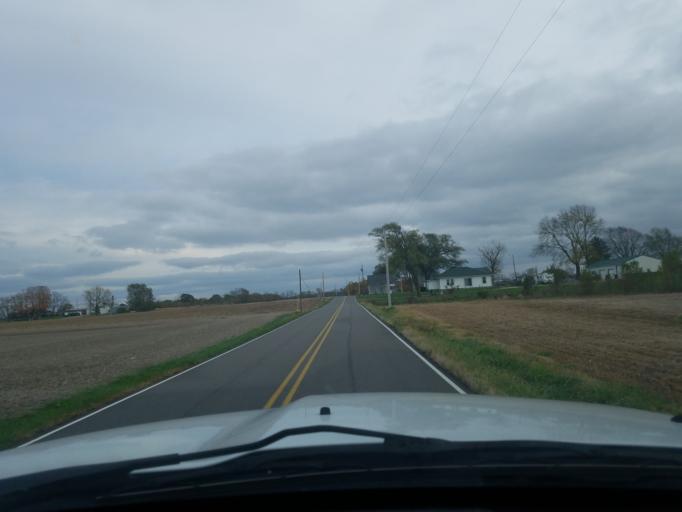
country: US
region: Indiana
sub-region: Shelby County
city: Shelbyville
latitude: 39.5397
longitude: -85.8497
